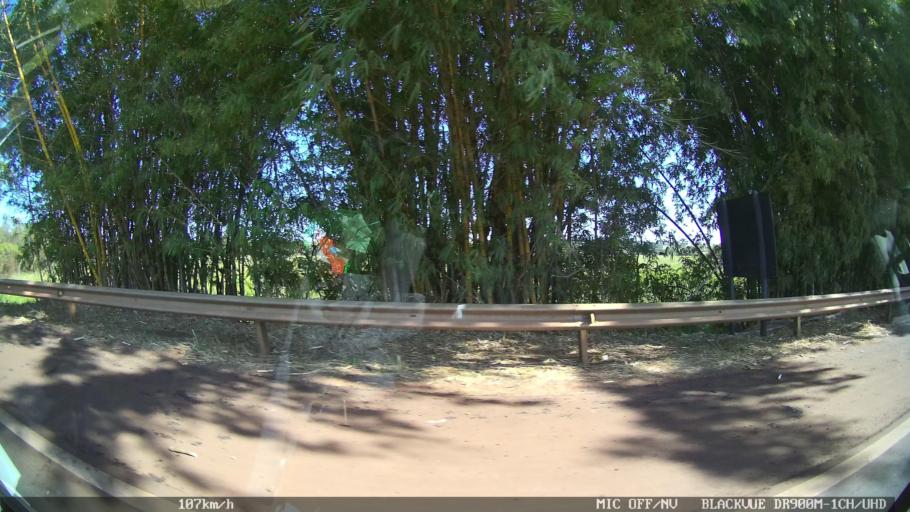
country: BR
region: Sao Paulo
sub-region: Olimpia
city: Olimpia
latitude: -20.7019
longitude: -48.8881
